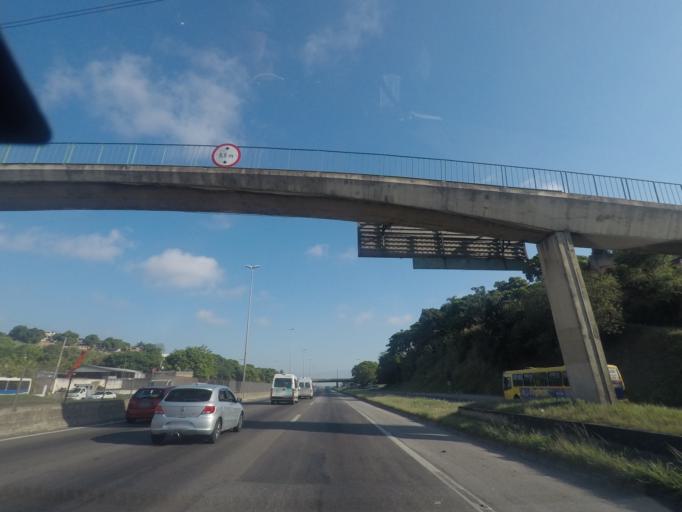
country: BR
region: Rio de Janeiro
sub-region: Duque De Caxias
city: Duque de Caxias
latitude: -22.7665
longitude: -43.2865
